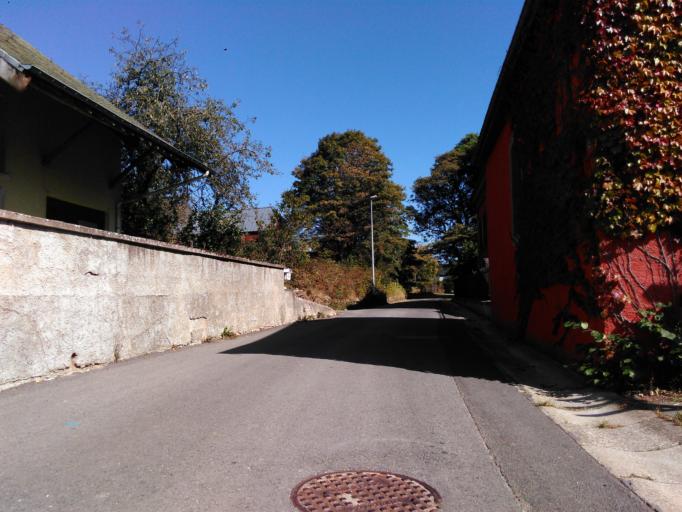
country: LU
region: Diekirch
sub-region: Canton de Redange
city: Rambrouch
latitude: 49.8294
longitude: 5.8419
